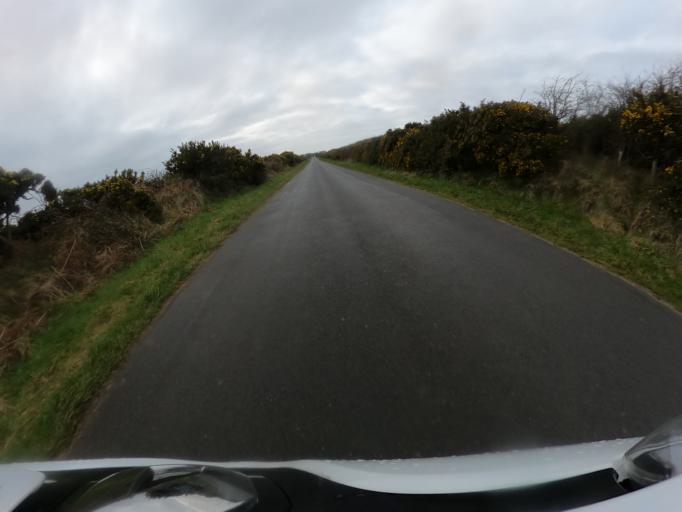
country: IM
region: Ramsey
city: Ramsey
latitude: 54.3518
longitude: -4.5291
